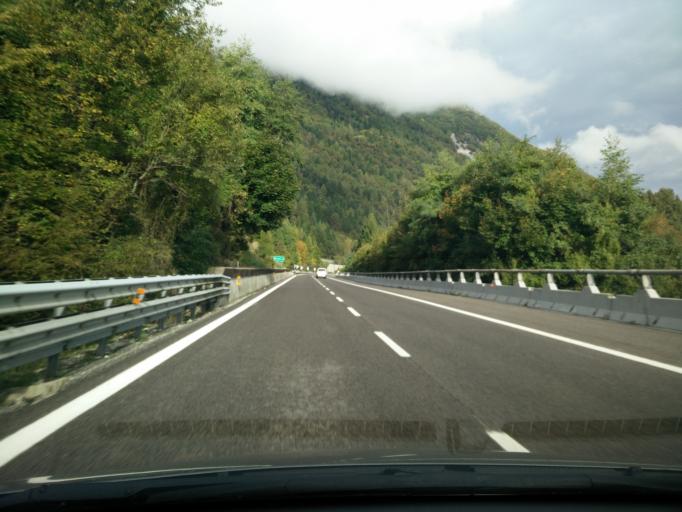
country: IT
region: Veneto
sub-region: Provincia di Belluno
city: Farra d'Alpago
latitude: 46.0919
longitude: 12.3278
